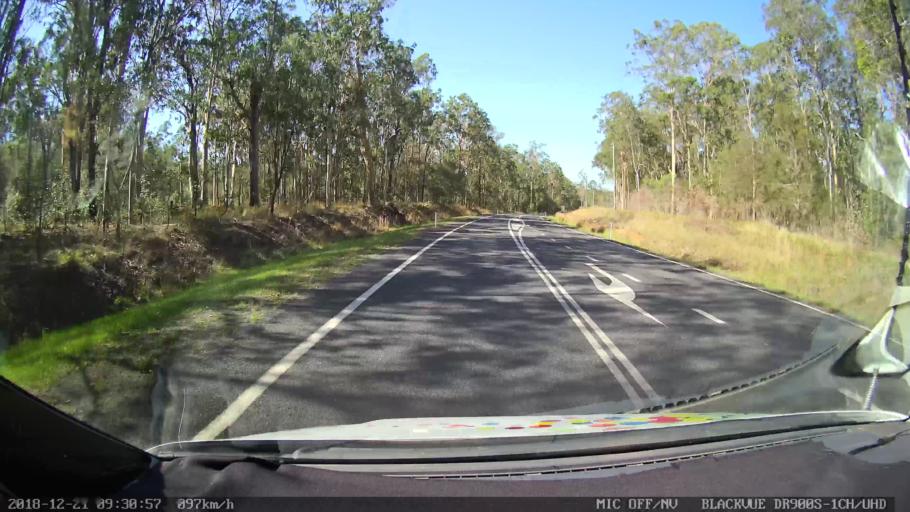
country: AU
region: New South Wales
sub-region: Clarence Valley
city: Maclean
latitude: -29.4542
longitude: 152.9937
